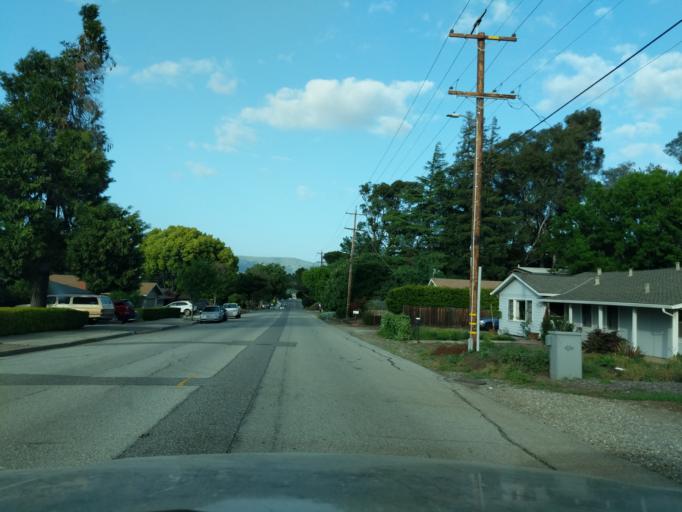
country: US
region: California
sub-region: Santa Clara County
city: Morgan Hill
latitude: 37.1218
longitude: -121.6612
